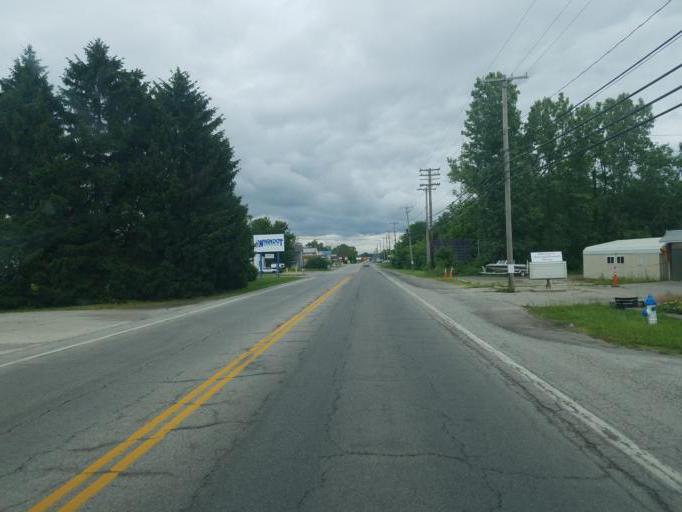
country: US
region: Ohio
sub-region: Marion County
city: Marion
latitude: 40.6092
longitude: -83.1304
